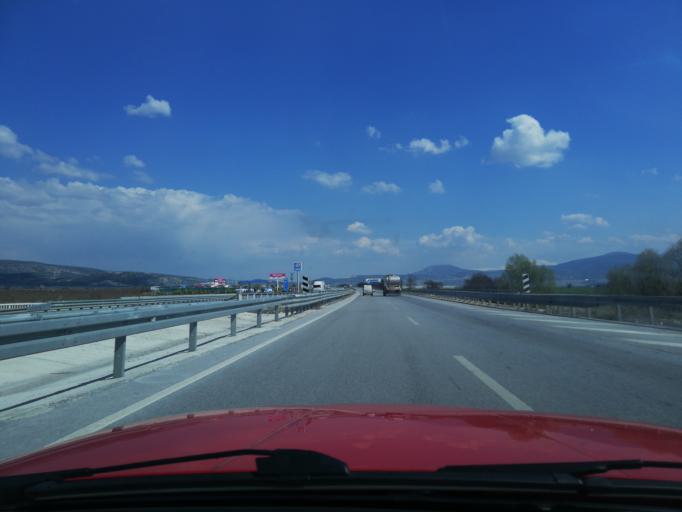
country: TR
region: Isparta
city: Keciborlu
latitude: 37.8990
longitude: 30.3452
